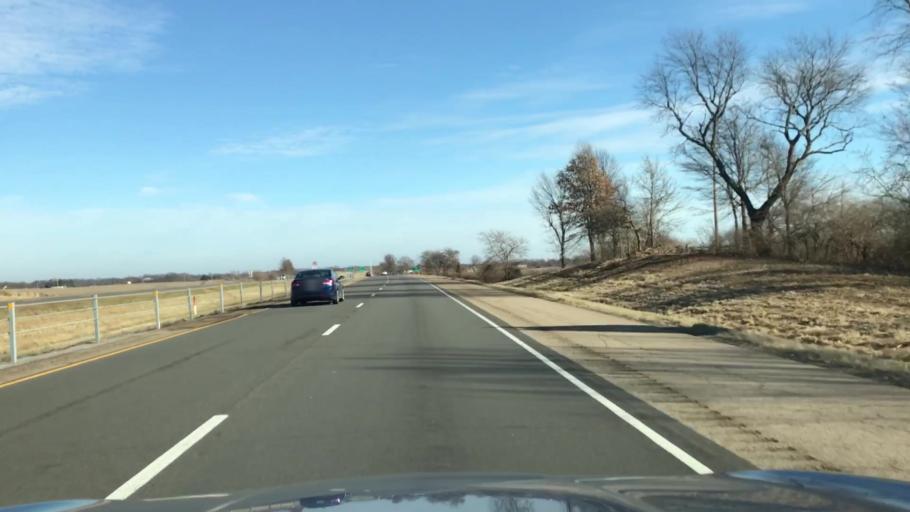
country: US
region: Illinois
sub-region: Madison County
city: Maryville
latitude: 38.7513
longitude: -89.9226
